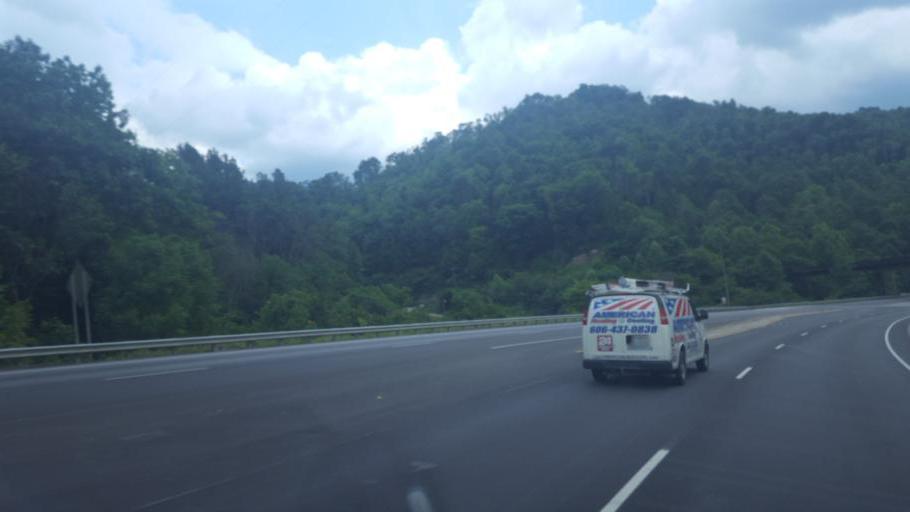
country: US
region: Kentucky
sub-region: Pike County
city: Pikeville
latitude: 37.3458
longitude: -82.5475
